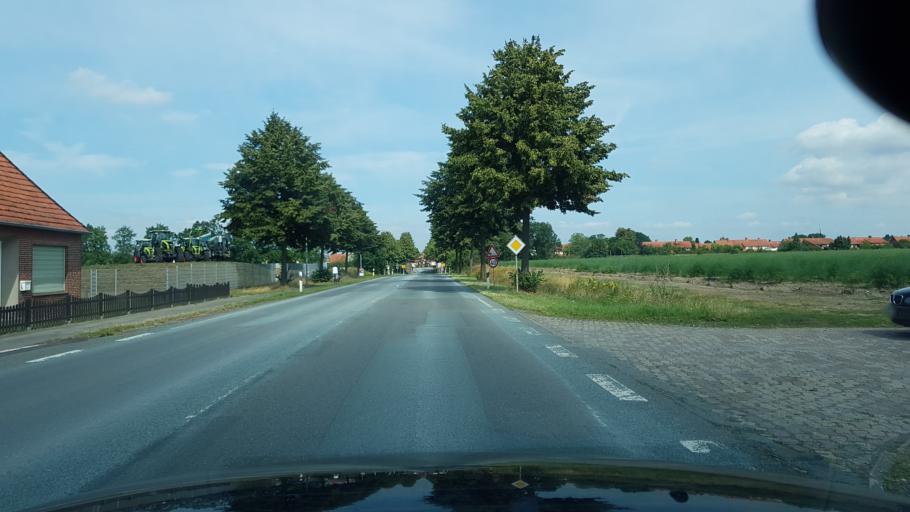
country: DE
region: Lower Saxony
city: Sulingen
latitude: 52.6734
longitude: 8.8074
